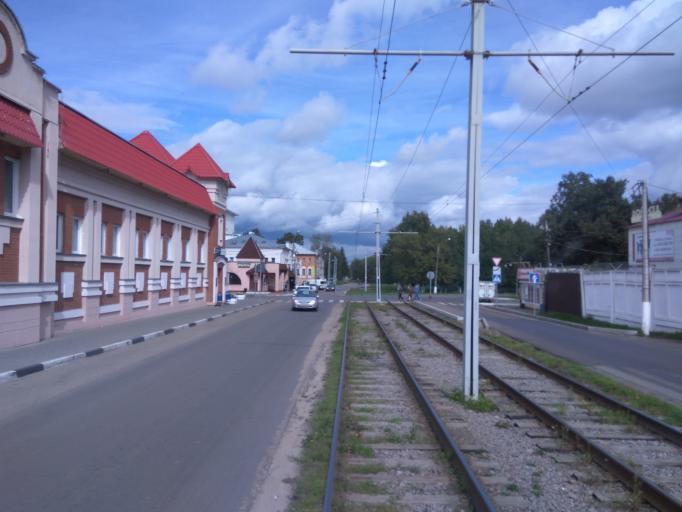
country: RU
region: Moskovskaya
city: Kolomna
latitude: 55.0983
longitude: 38.7748
